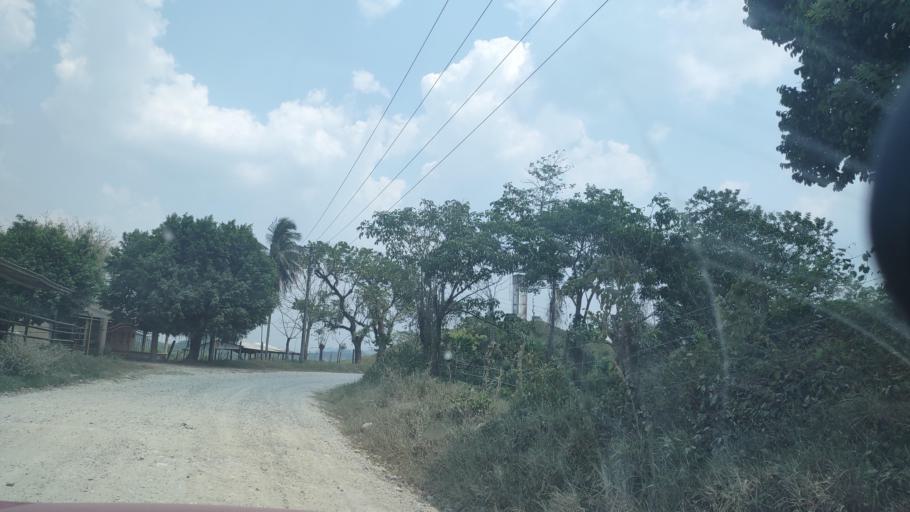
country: MX
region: Tabasco
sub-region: Huimanguillo
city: Francisco Rueda
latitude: 17.6123
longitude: -93.9137
